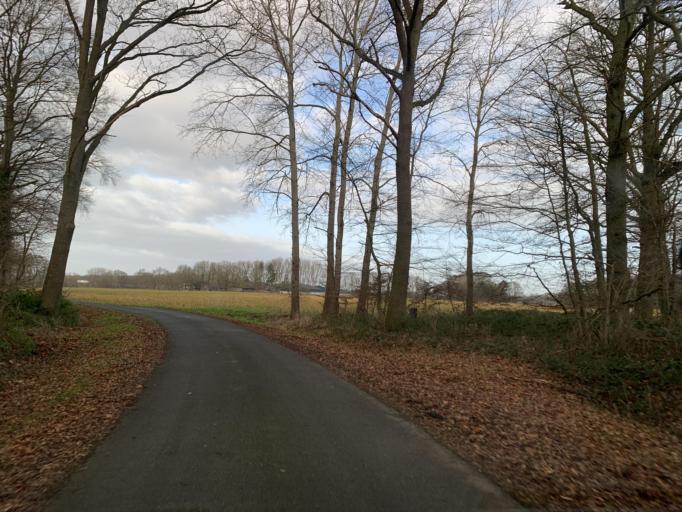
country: DE
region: North Rhine-Westphalia
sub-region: Regierungsbezirk Munster
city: Greven
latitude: 52.0496
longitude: 7.6267
